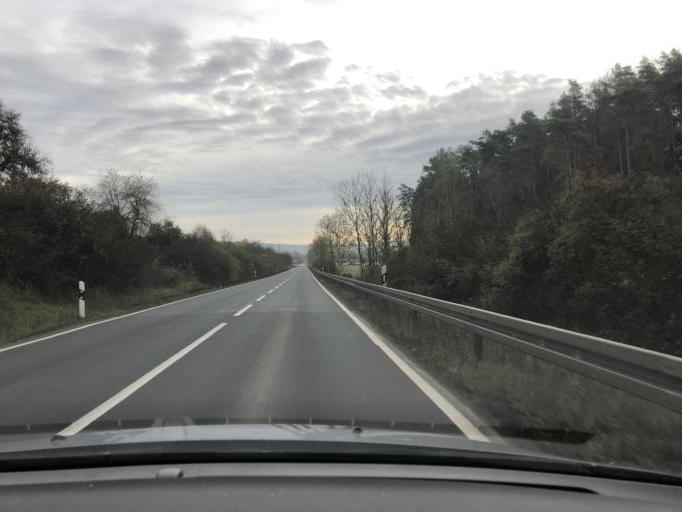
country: DE
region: Thuringia
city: Hildburghausen
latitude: 50.4185
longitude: 10.7009
